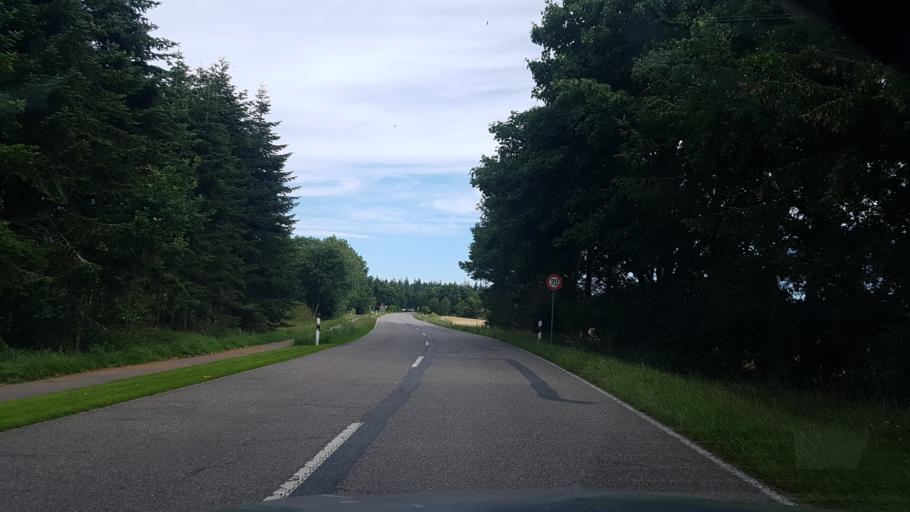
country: DE
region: Schleswig-Holstein
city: Ladelund
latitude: 54.8506
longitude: 9.0371
